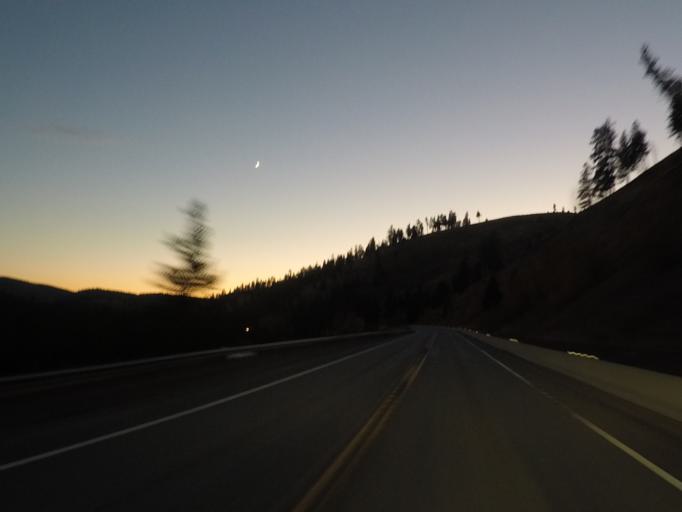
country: US
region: Montana
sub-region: Missoula County
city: Seeley Lake
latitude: 47.0240
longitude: -113.3130
